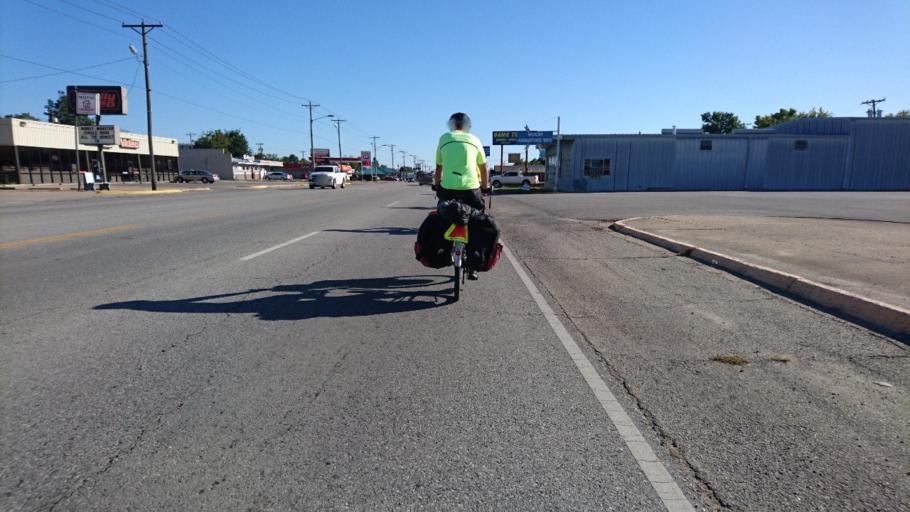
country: US
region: Oklahoma
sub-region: Ottawa County
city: Miami
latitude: 36.8976
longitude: -94.8776
